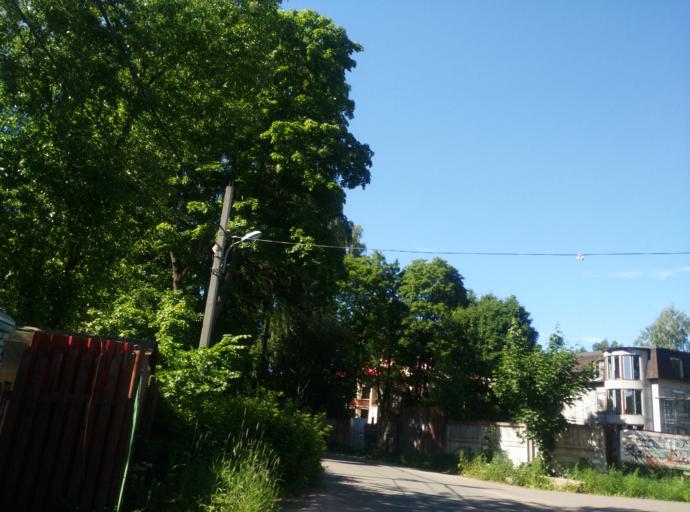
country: RU
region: St.-Petersburg
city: Ozerki
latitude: 60.0336
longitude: 30.3107
